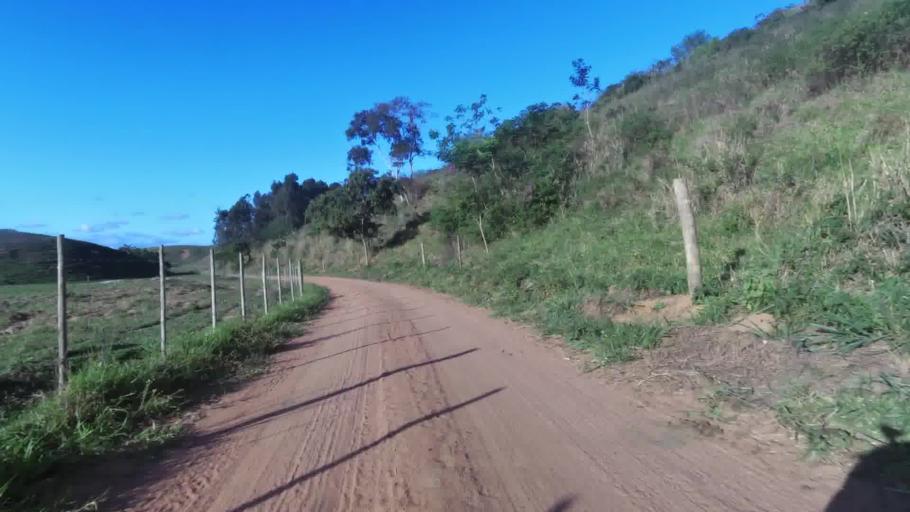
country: BR
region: Espirito Santo
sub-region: Marataizes
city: Marataizes
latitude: -21.1424
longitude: -41.0224
